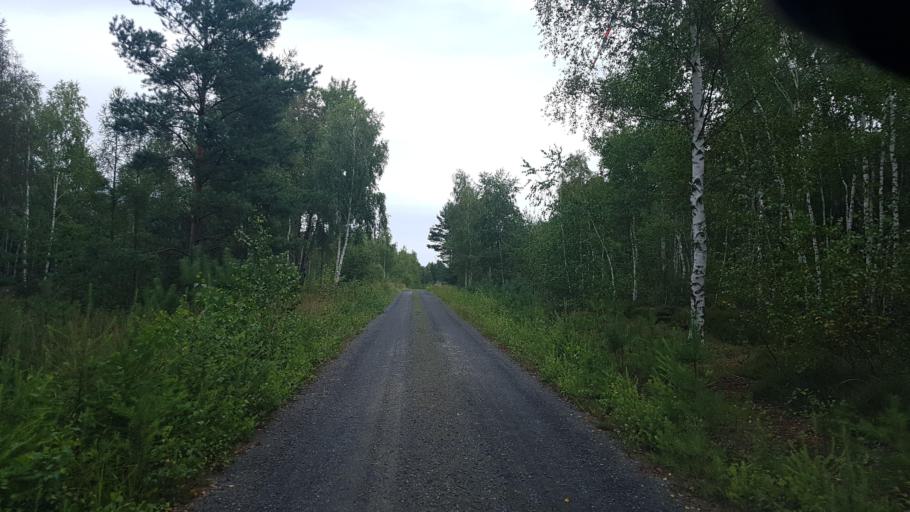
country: DE
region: Brandenburg
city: Grossraschen
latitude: 51.6218
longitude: 13.9689
